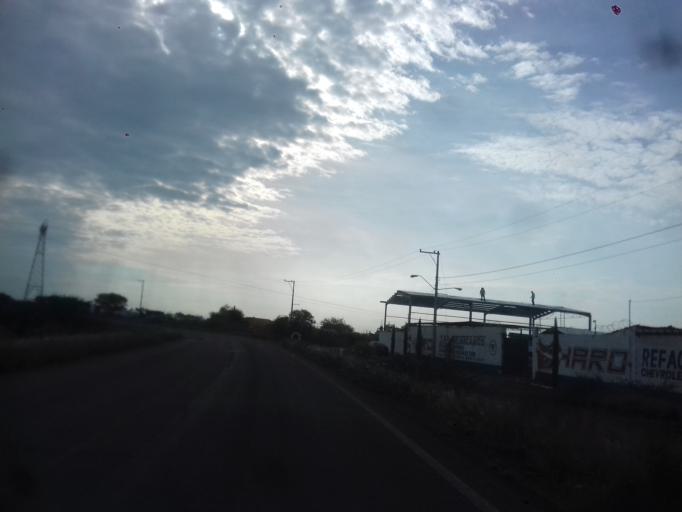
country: MX
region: Aguascalientes
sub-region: Aguascalientes
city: San Sebastian [Fraccionamiento]
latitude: 21.7906
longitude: -102.2281
